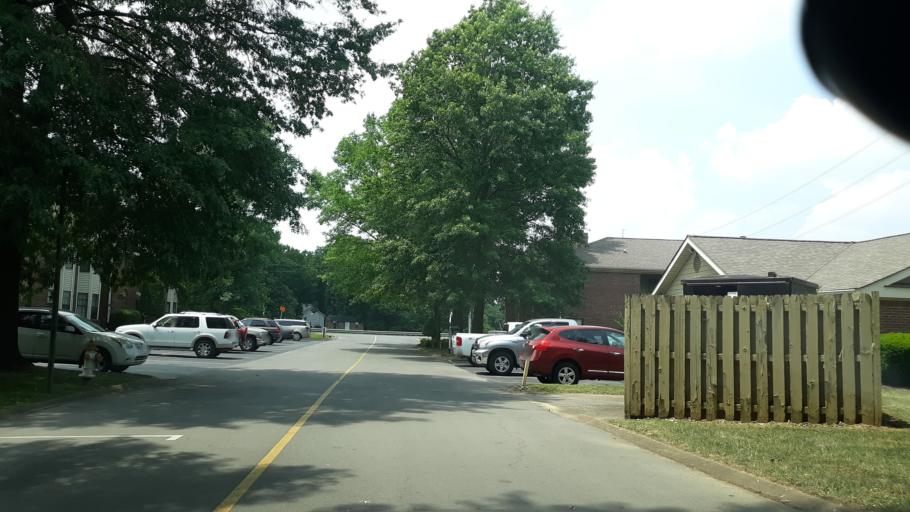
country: US
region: Tennessee
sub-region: Davidson County
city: Lakewood
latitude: 36.1824
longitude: -86.6104
